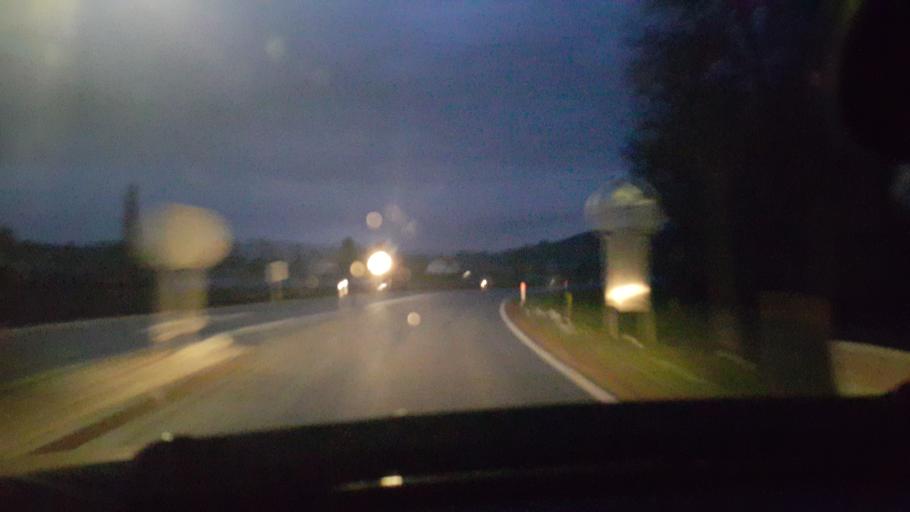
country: AT
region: Styria
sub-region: Politischer Bezirk Leibnitz
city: Oberhaag
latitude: 46.6885
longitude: 15.3288
